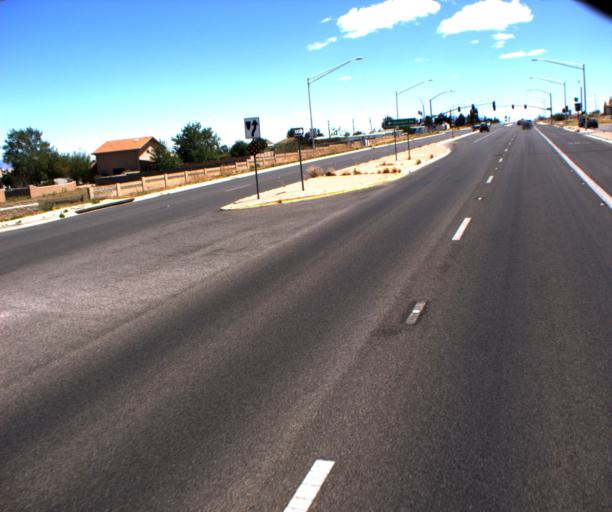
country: US
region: Arizona
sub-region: Cochise County
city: Sierra Vista Southeast
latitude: 31.4391
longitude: -110.2495
